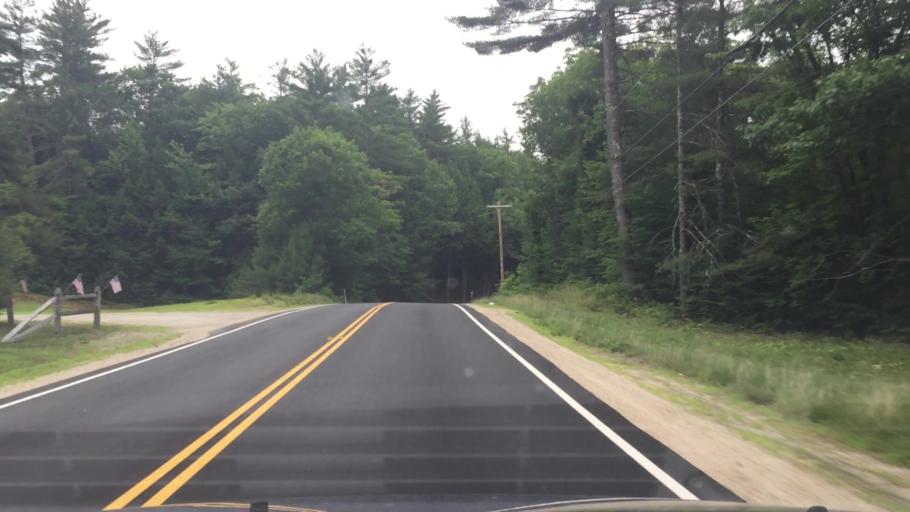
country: US
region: New Hampshire
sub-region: Carroll County
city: Freedom
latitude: 43.8588
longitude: -71.0879
